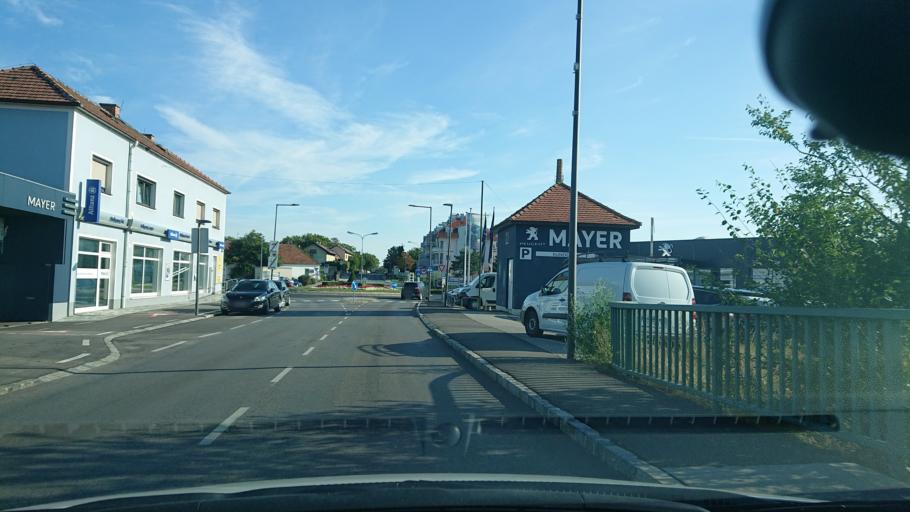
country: AT
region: Lower Austria
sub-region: Politischer Bezirk Baden
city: Leobersdorf
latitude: 47.9342
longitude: 16.2187
